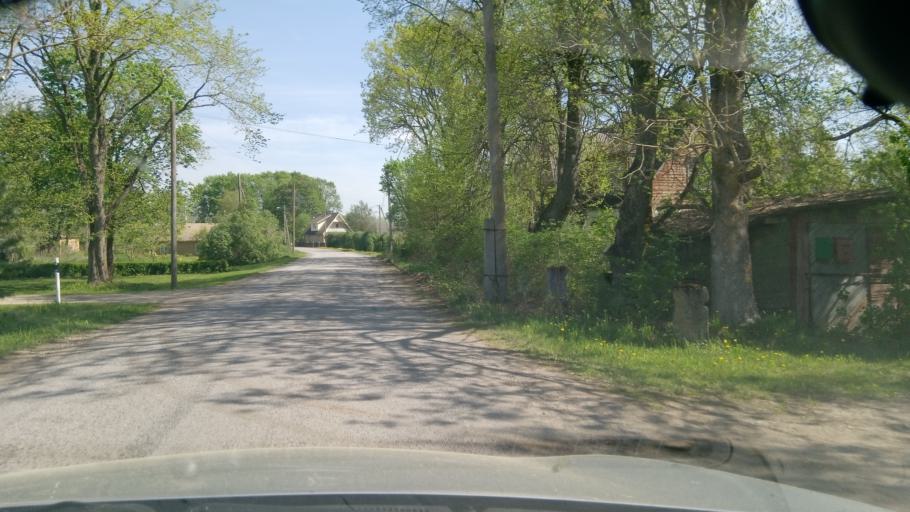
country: EE
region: Laeaene-Virumaa
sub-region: Tapa vald
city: Tapa
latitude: 59.1969
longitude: 25.8438
